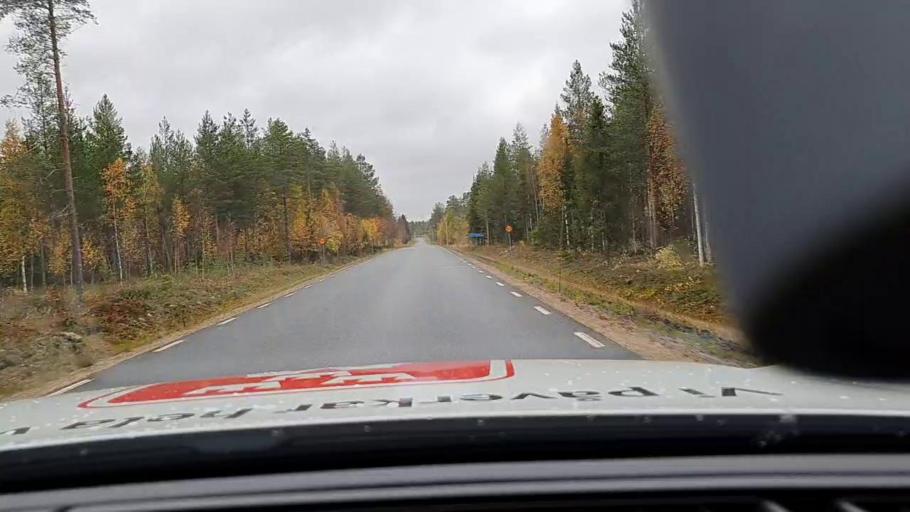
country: SE
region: Norrbotten
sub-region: Haparanda Kommun
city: Haparanda
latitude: 65.9422
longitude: 23.8013
